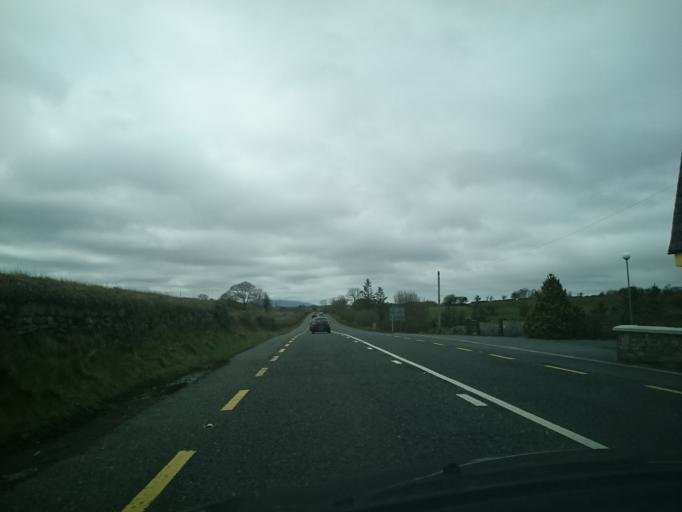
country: IE
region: Connaught
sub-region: Maigh Eo
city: Westport
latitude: 53.8136
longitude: -9.4071
